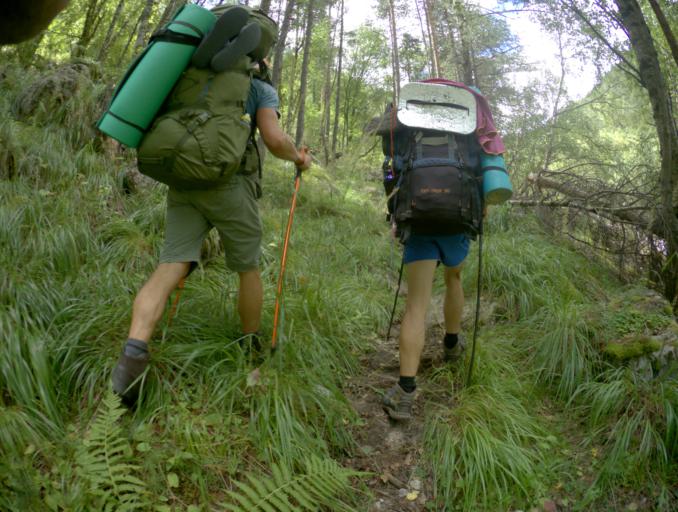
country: RU
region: Karachayevo-Cherkesiya
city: Uchkulan
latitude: 43.3562
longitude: 42.1813
